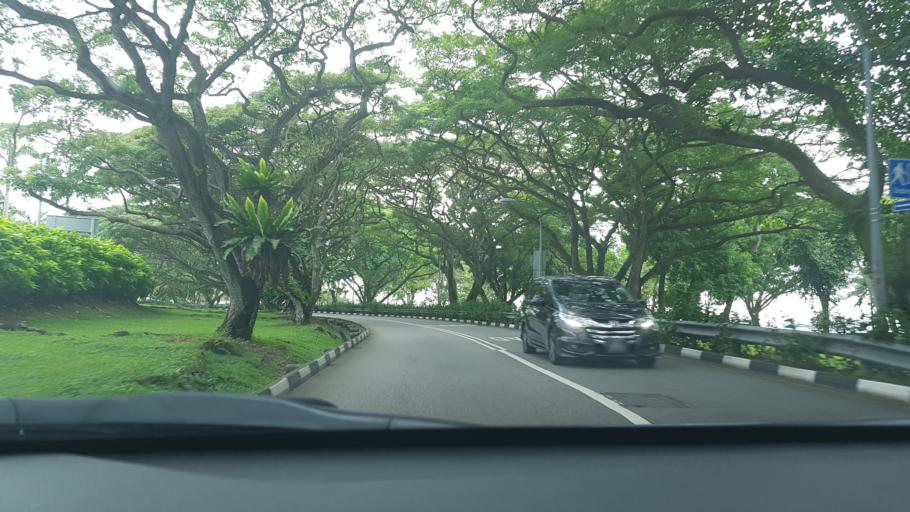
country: SG
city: Singapore
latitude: 1.3001
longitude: 103.9092
